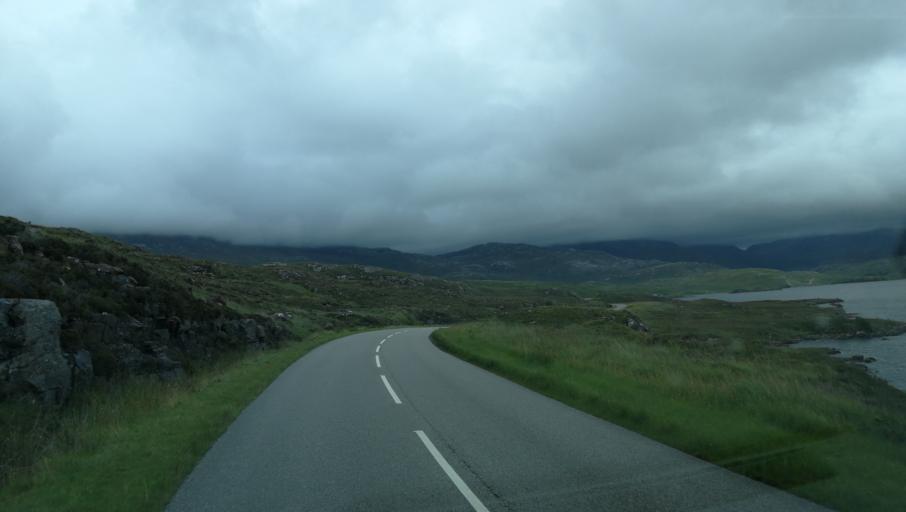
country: GB
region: Scotland
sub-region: Highland
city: Ullapool
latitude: 58.1773
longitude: -5.0262
